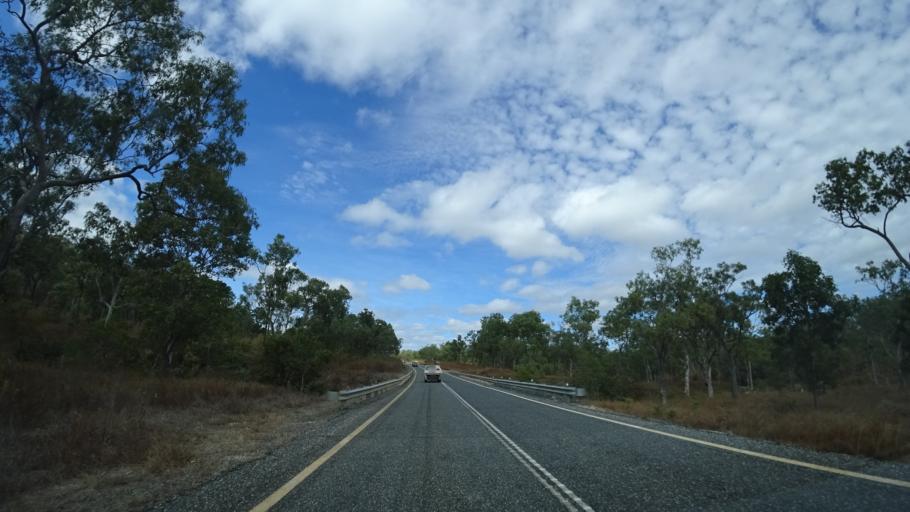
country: AU
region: Queensland
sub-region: Cairns
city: Port Douglas
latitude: -16.3540
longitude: 144.7269
